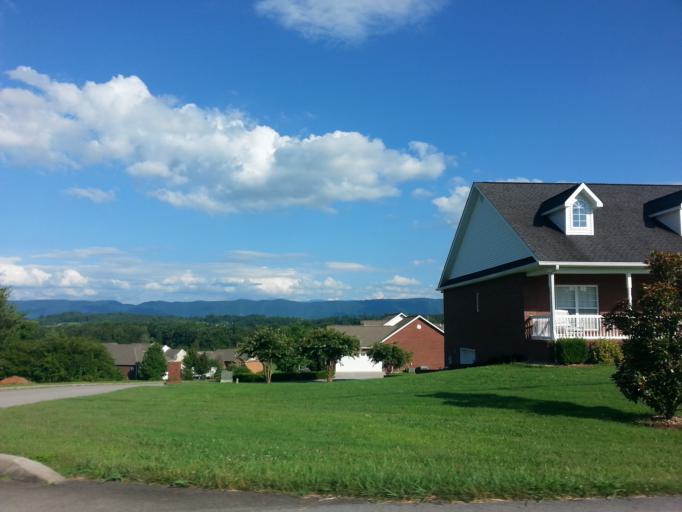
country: US
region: Tennessee
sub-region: Loudon County
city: Greenback
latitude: 35.6761
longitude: -84.0563
